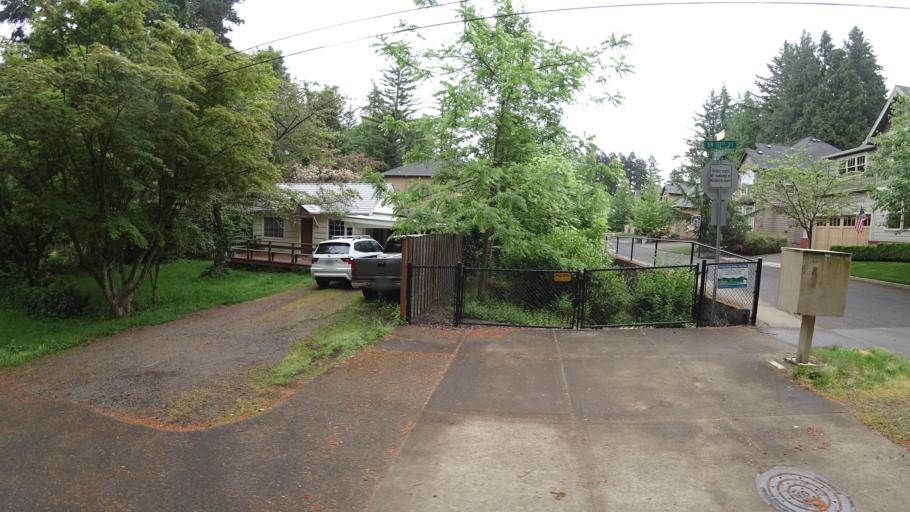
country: US
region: Oregon
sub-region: Washington County
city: Garden Home-Whitford
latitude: 45.4686
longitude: -122.7604
